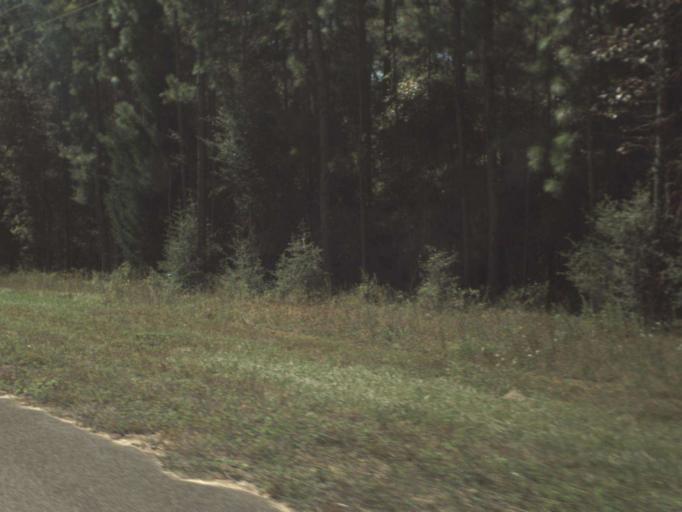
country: US
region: Florida
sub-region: Walton County
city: DeFuniak Springs
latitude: 30.8826
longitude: -86.1252
